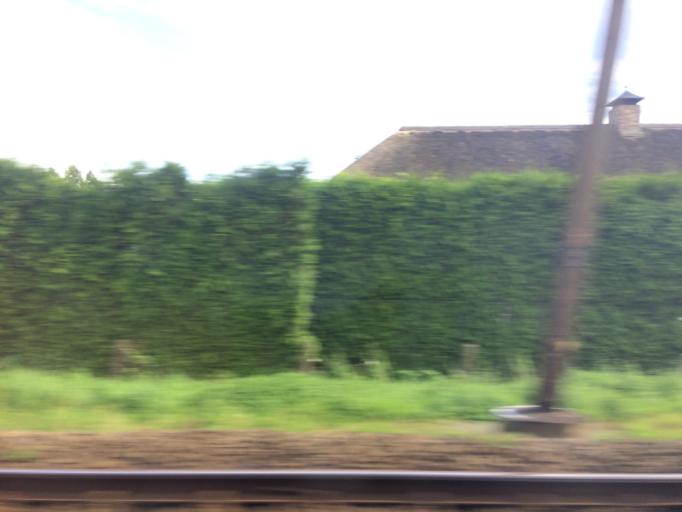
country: NL
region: North Brabant
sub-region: Gemeente Oss
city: Berghem
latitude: 51.7672
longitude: 5.5648
